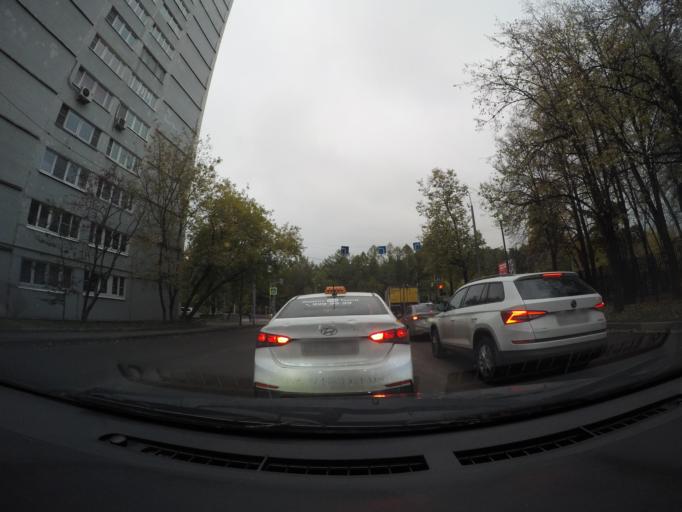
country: RU
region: Moskovskaya
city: Izmaylovo
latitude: 55.7651
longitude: 37.7903
